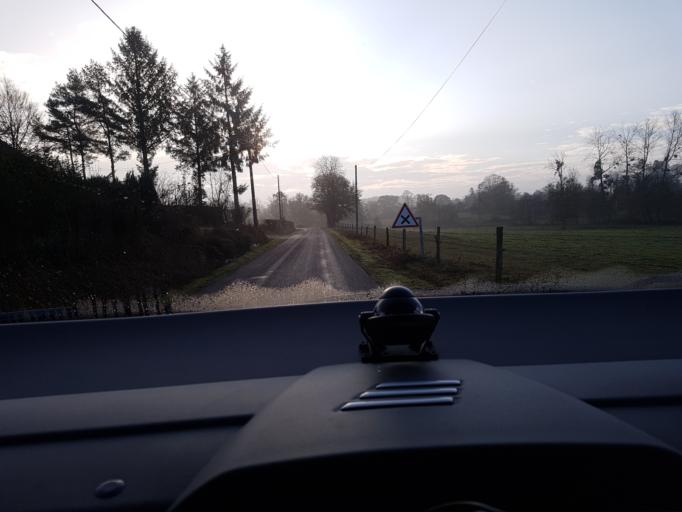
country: FR
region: Lower Normandy
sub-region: Departement de l'Orne
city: Champsecret
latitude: 48.6389
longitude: -0.5836
